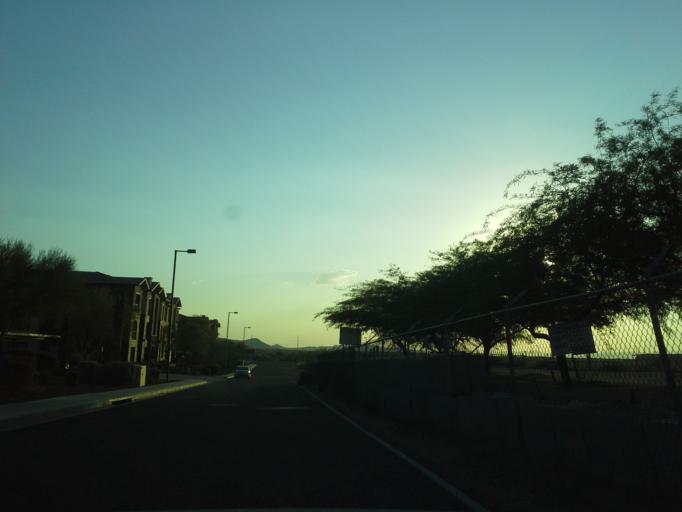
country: US
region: Arizona
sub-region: Maricopa County
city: Anthem
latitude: 33.7548
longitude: -112.1057
